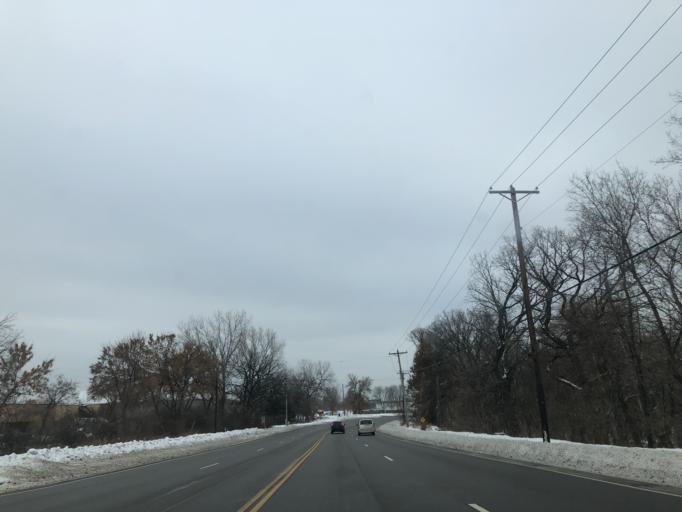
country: US
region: Minnesota
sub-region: Ramsey County
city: New Brighton
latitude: 45.0772
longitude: -93.1882
